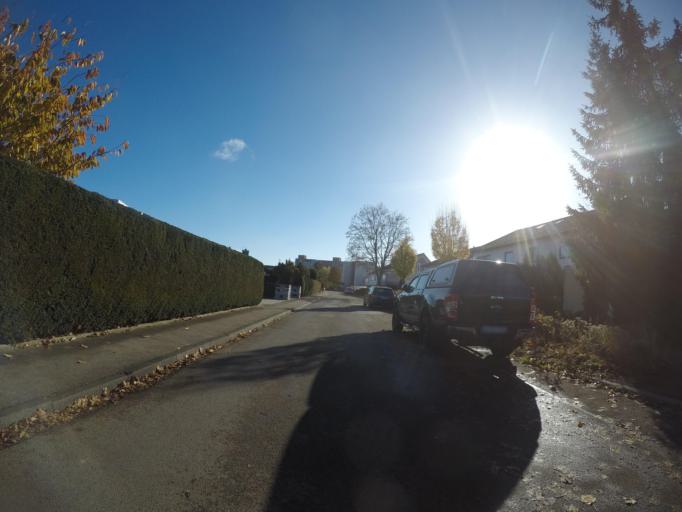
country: DE
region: Baden-Wuerttemberg
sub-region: Tuebingen Region
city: Dornstadt
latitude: 48.4691
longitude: 9.9349
